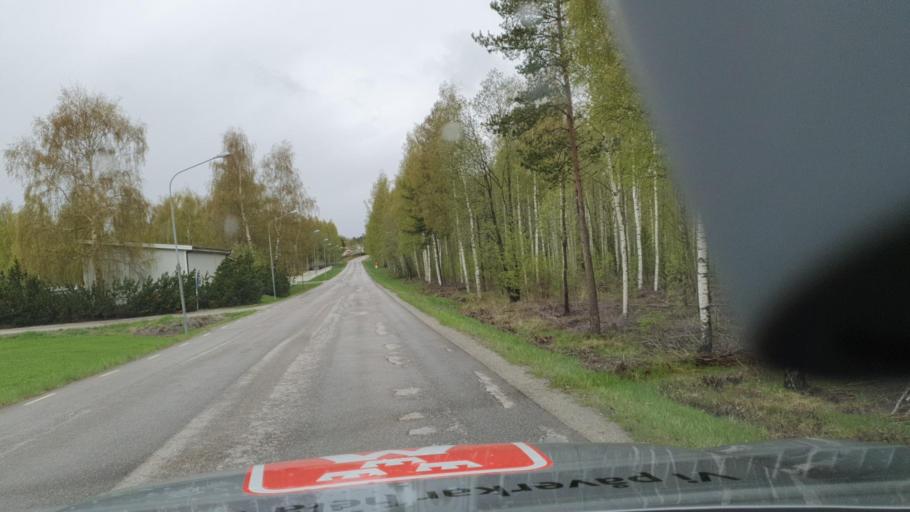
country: SE
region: Vaesternorrland
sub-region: OErnskoeldsviks Kommun
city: Ornskoldsvik
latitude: 63.2958
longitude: 18.6100
